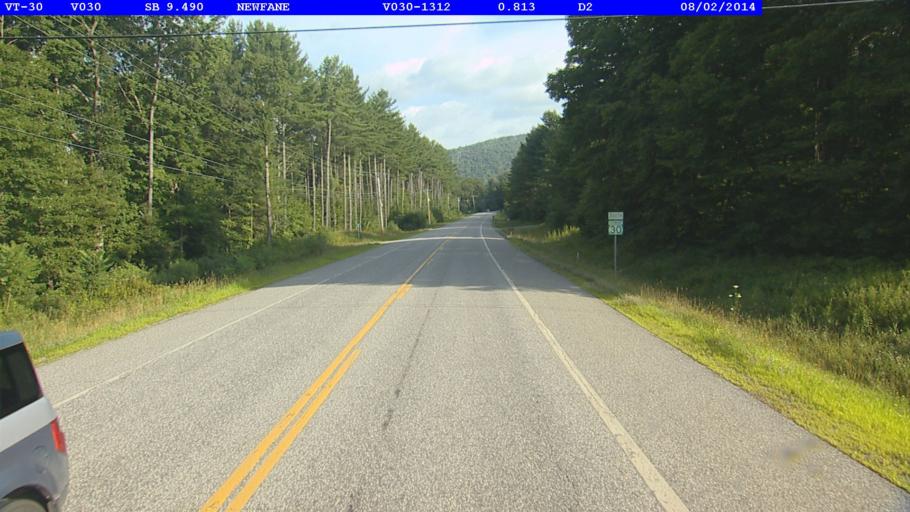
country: US
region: Vermont
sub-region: Windham County
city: Newfane
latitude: 42.9572
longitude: -72.6497
